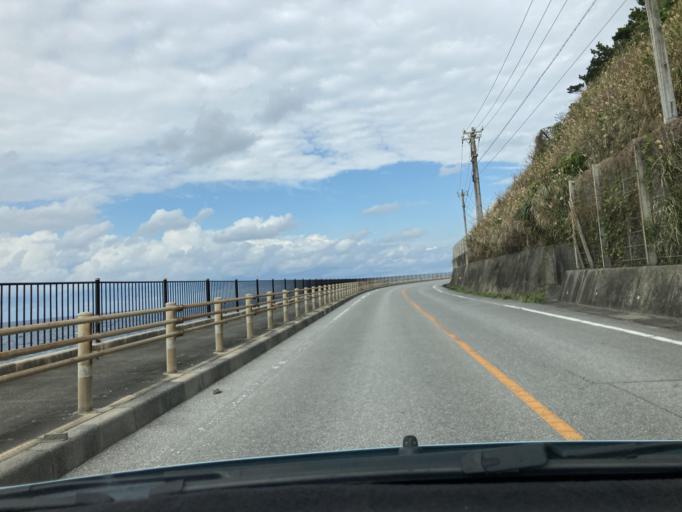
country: JP
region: Okinawa
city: Nago
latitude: 26.7953
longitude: 128.2255
